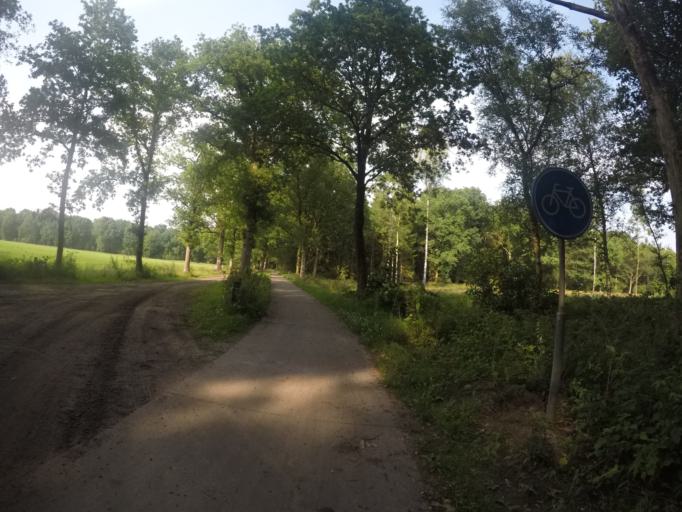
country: NL
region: Friesland
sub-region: Gemeente Weststellingwerf
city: Noordwolde
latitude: 52.8864
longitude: 6.2160
